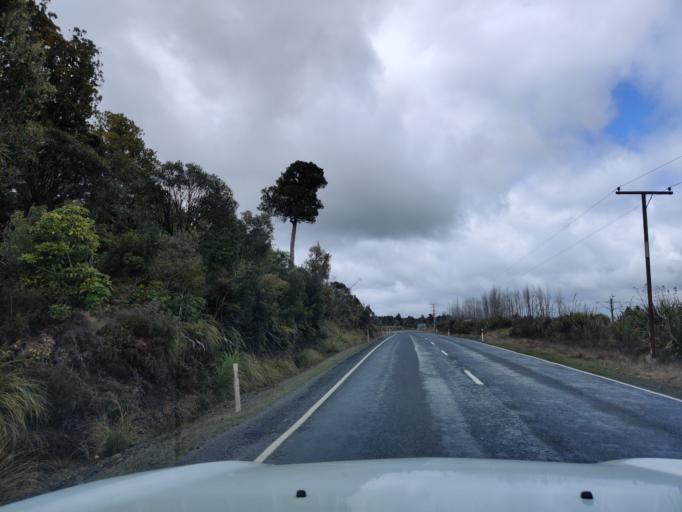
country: NZ
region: Manawatu-Wanganui
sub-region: Ruapehu District
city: Waiouru
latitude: -39.2535
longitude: 175.3880
